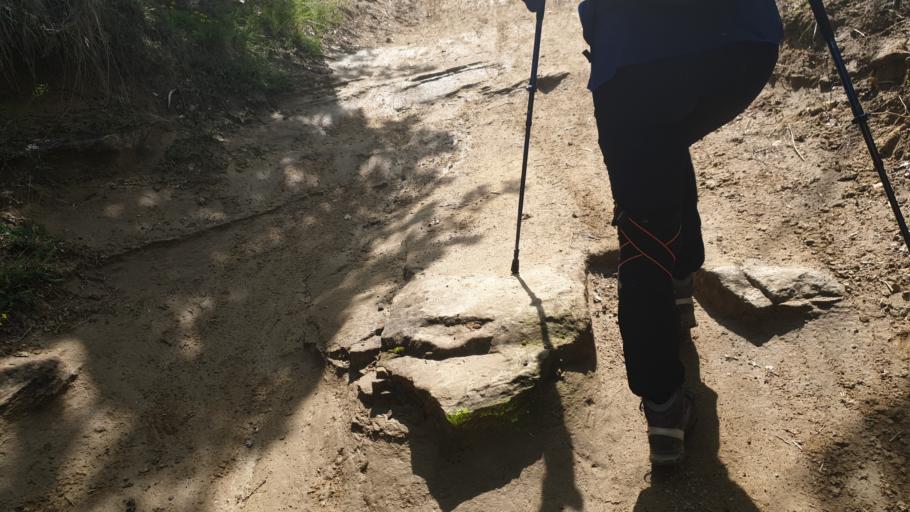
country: IT
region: Emilia-Romagna
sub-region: Provincia di Bologna
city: Vado
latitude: 44.3543
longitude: 11.2900
